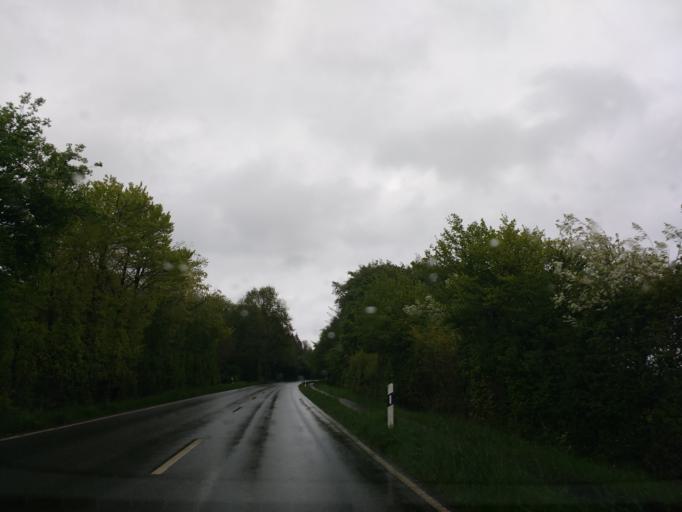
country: DE
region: Schleswig-Holstein
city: Damp
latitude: 54.5776
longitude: 9.9725
